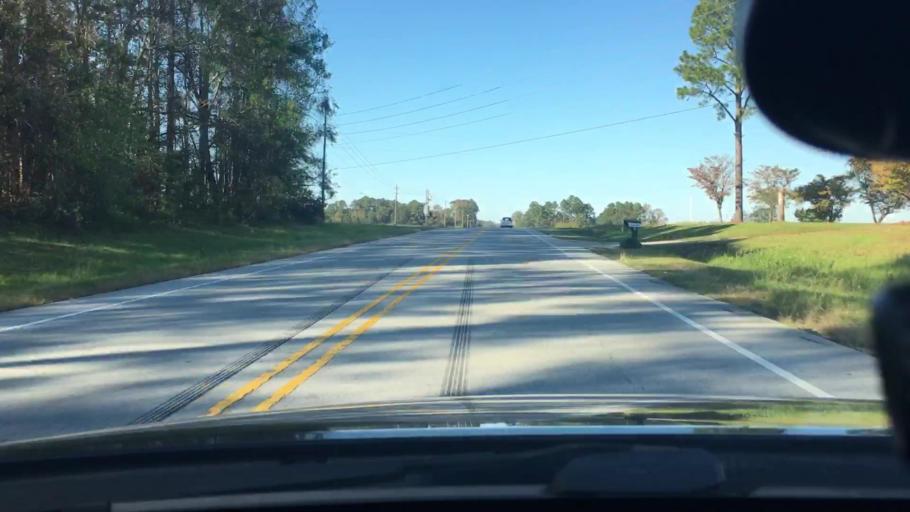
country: US
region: North Carolina
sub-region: Craven County
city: Trent Woods
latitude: 35.1811
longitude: -77.1315
